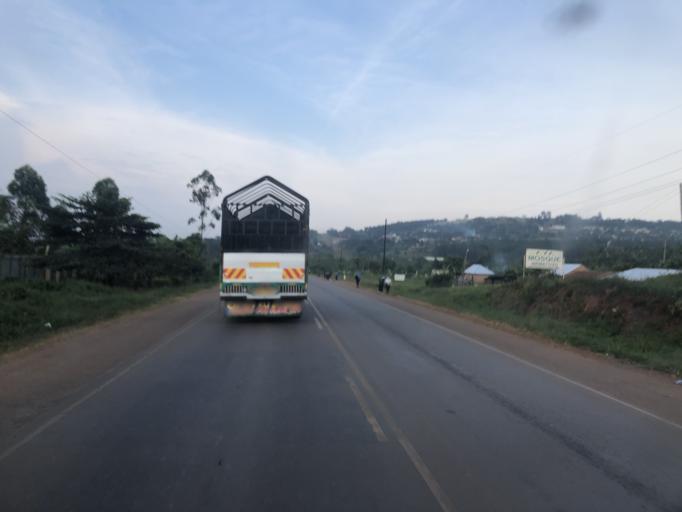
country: UG
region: Central Region
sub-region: Mpigi District
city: Mpigi
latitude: 0.2502
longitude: 32.3900
